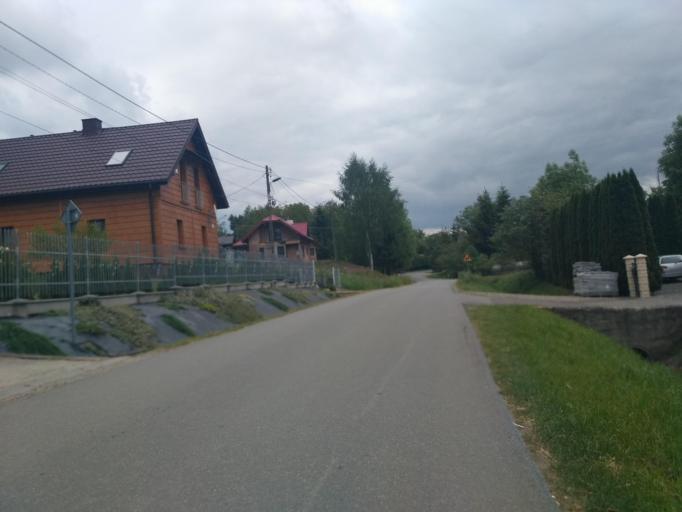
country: PL
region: Subcarpathian Voivodeship
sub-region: Powiat krosnienski
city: Jedlicze
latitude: 49.6883
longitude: 21.6429
